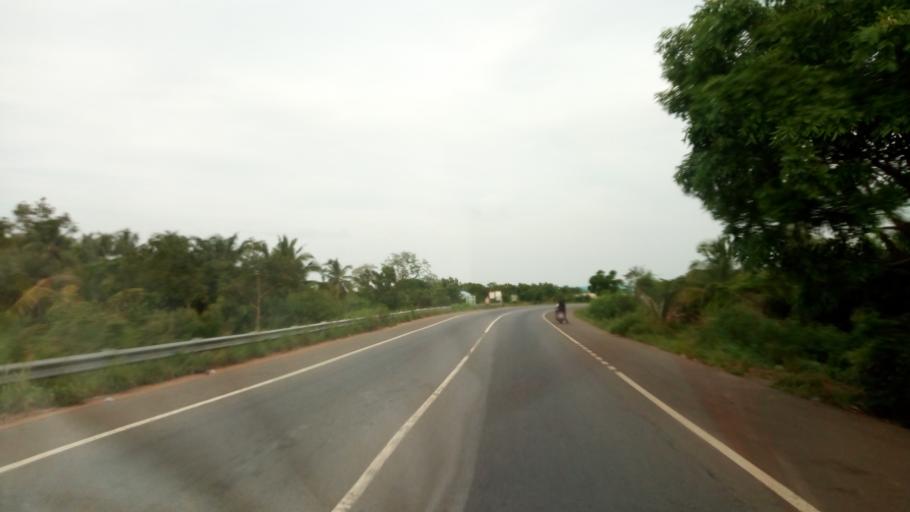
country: GH
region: Volta
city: Keta
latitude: 6.0515
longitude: 0.9729
